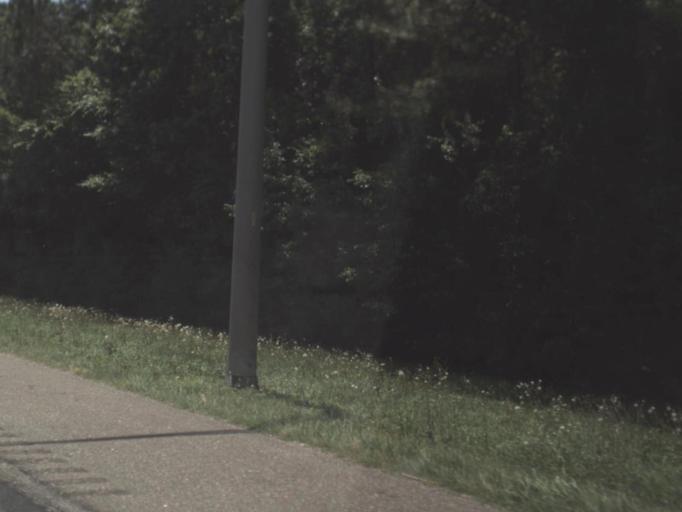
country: US
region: Florida
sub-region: Duval County
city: Jacksonville
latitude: 30.3785
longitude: -81.7610
